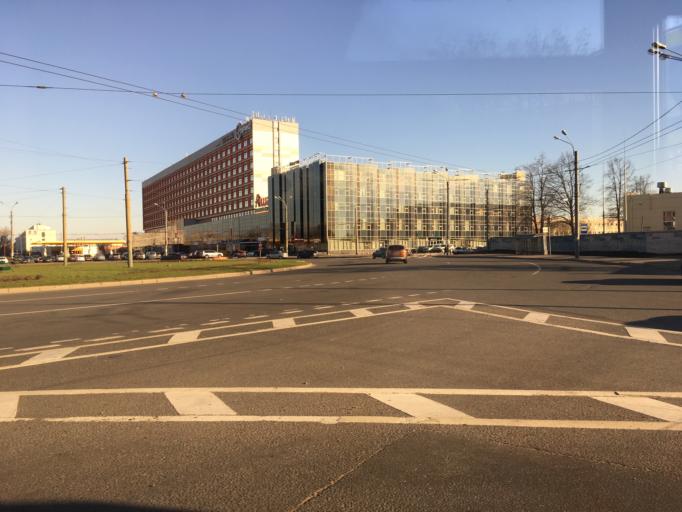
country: RU
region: St.-Petersburg
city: Centralniy
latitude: 59.9019
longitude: 30.3996
